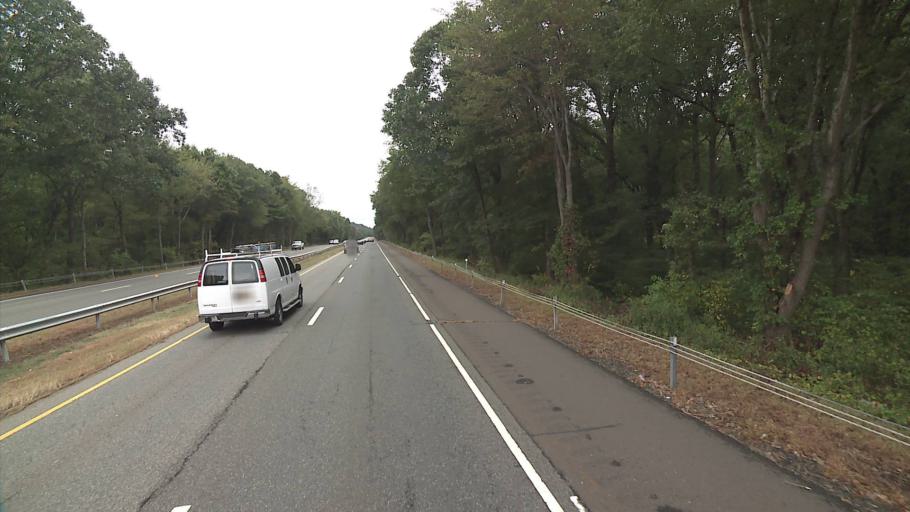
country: US
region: Connecticut
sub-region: New Haven County
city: North Haven
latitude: 41.4185
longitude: -72.8557
